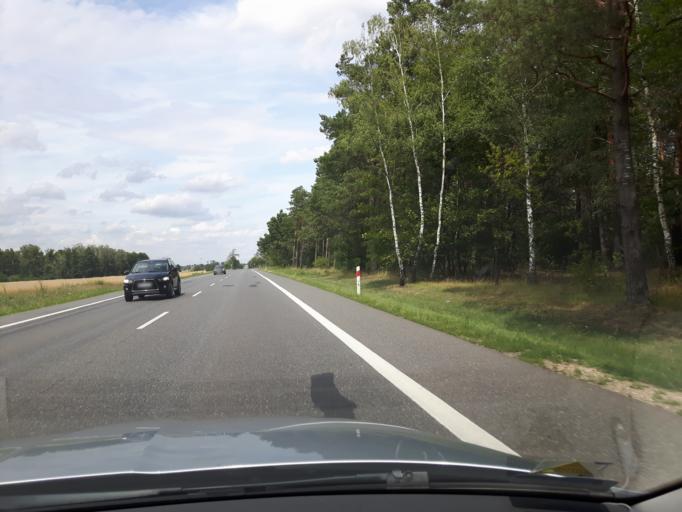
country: PL
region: Masovian Voivodeship
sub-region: Powiat mlawski
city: Strzegowo
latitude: 52.9227
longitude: 20.2862
